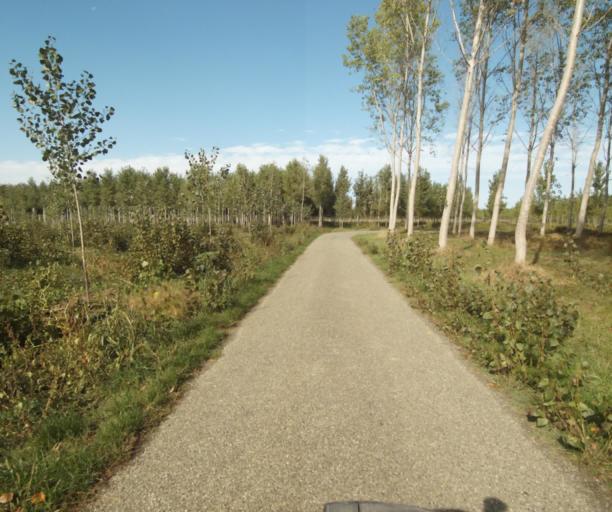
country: FR
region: Midi-Pyrenees
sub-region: Departement du Tarn-et-Garonne
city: Finhan
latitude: 43.9023
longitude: 1.2157
